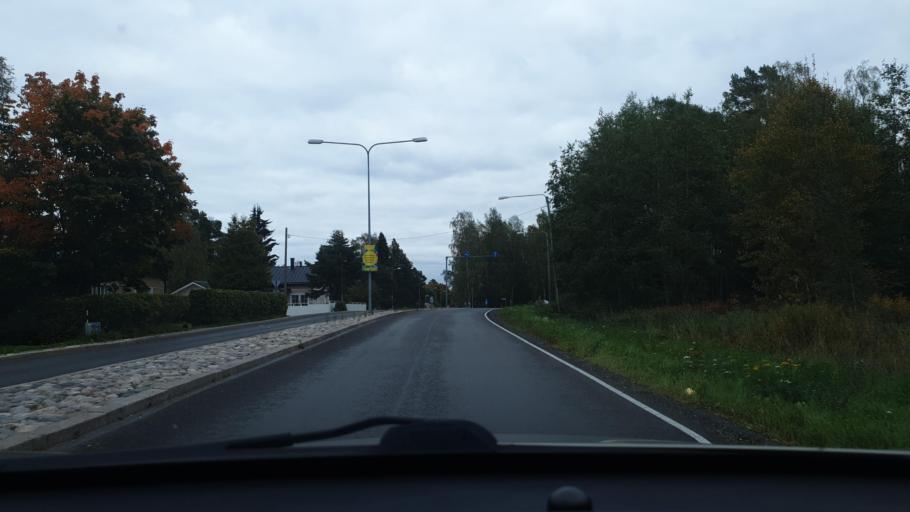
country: FI
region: Ostrobothnia
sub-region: Vaasa
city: Teeriniemi
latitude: 63.0901
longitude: 21.6855
